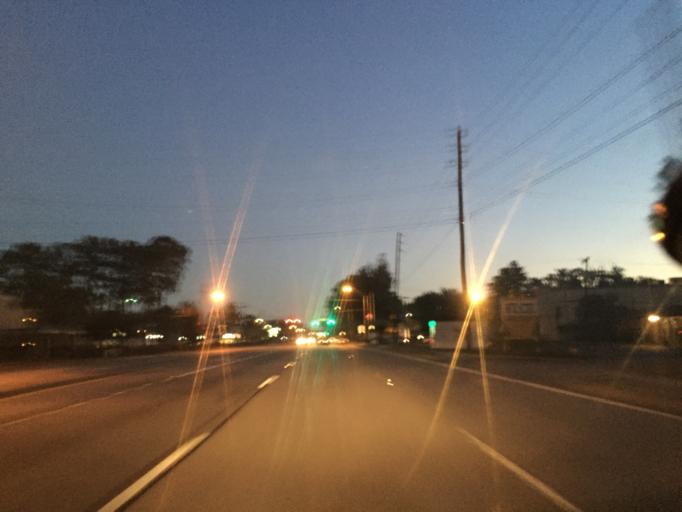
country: US
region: Georgia
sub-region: Chatham County
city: Isle of Hope
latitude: 32.0159
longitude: -81.1124
